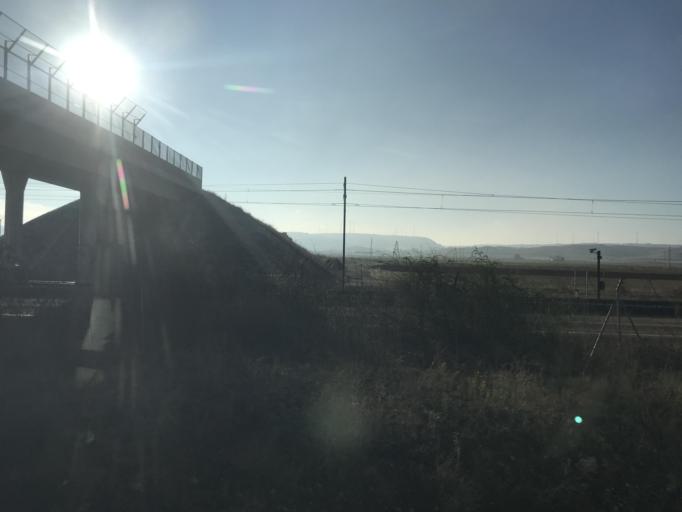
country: ES
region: Castille and Leon
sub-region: Provincia de Palencia
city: Quintana del Puente
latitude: 42.0656
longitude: -4.2210
